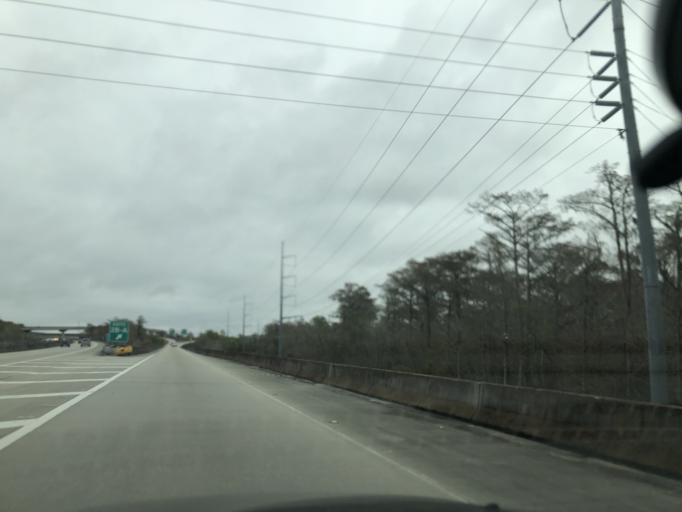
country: US
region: Louisiana
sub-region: Saint Charles Parish
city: Saint Rose
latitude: 29.9708
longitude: -90.3249
